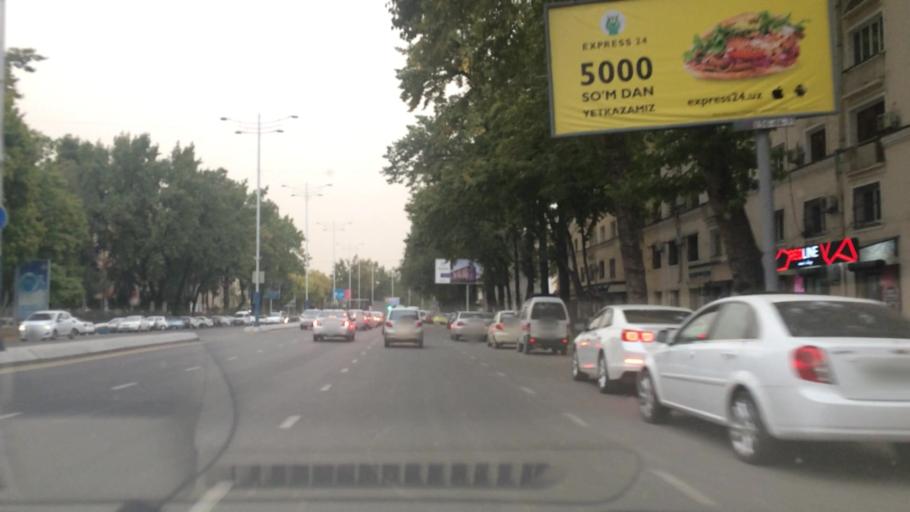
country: UZ
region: Toshkent Shahri
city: Tashkent
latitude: 41.2960
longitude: 69.2504
